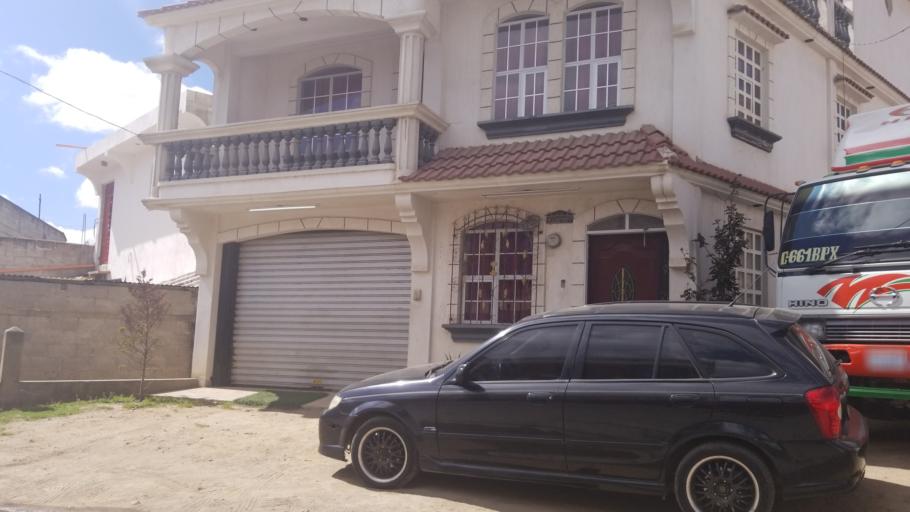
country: GT
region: Quetzaltenango
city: Quetzaltenango
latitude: 14.7997
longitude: -91.5450
